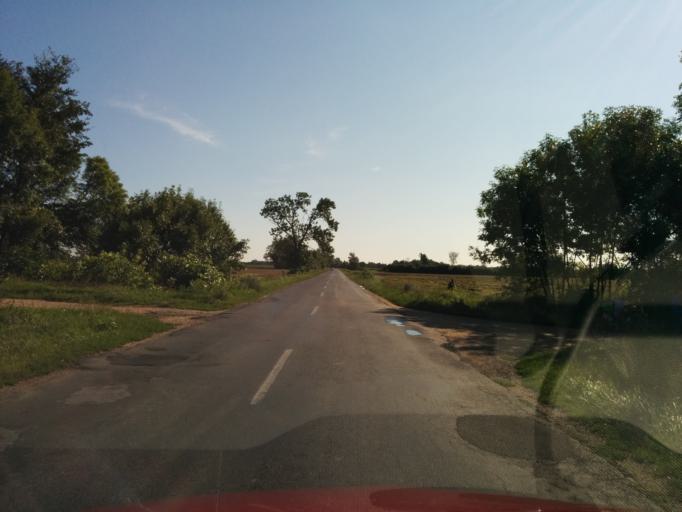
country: HU
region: Vas
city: Buk
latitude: 47.3694
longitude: 16.8443
